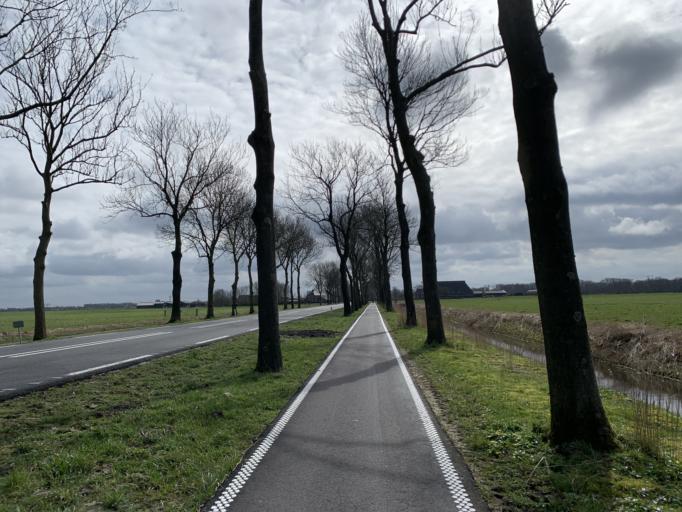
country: NL
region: Groningen
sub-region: Gemeente Groningen
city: Korrewegwijk
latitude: 53.2563
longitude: 6.5412
